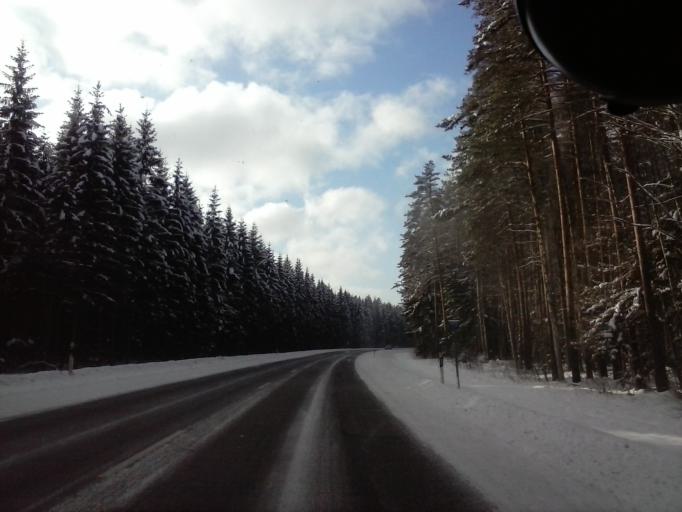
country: EE
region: Viljandimaa
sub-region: Moisakuela linn
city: Moisakula
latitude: 58.2232
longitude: 25.1042
